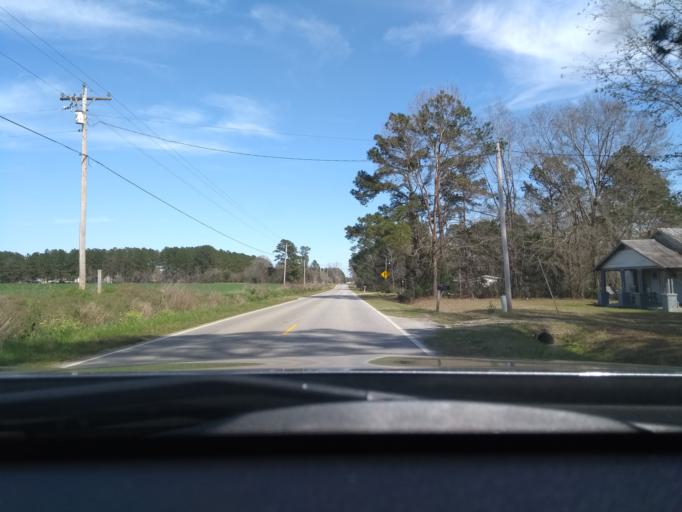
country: US
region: Georgia
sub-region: Bulloch County
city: Brooklet
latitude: 32.4197
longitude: -81.7081
